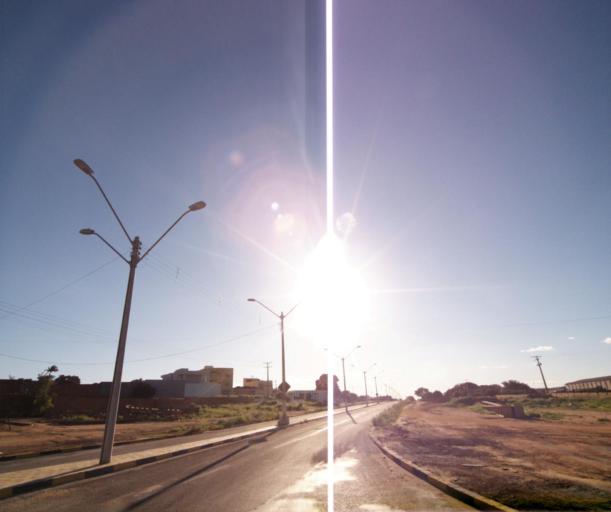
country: BR
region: Bahia
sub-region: Guanambi
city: Guanambi
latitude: -14.2099
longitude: -42.7807
